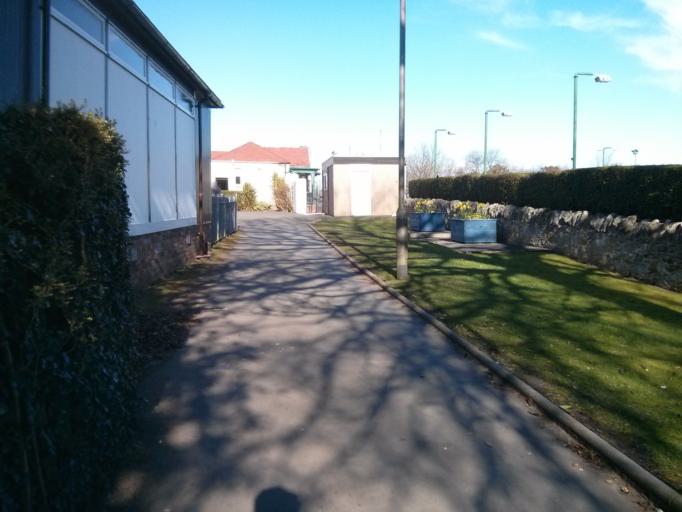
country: GB
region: Scotland
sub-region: Fife
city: Saint Andrews
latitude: 56.3397
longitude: -2.8038
